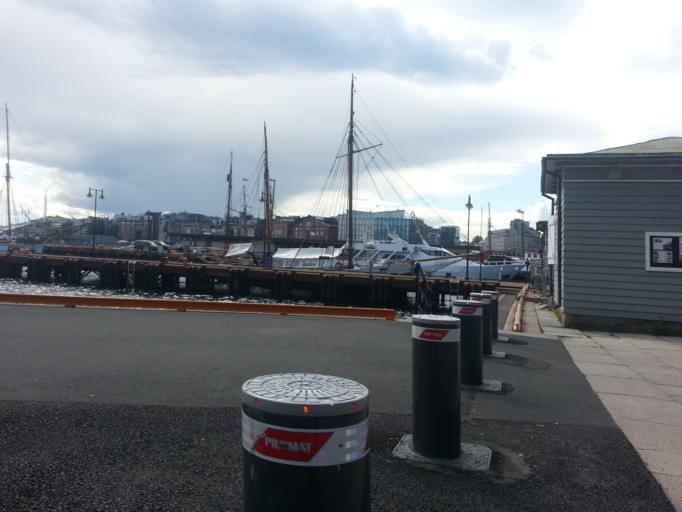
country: NO
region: Oslo
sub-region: Oslo
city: Oslo
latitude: 59.9100
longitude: 10.7345
